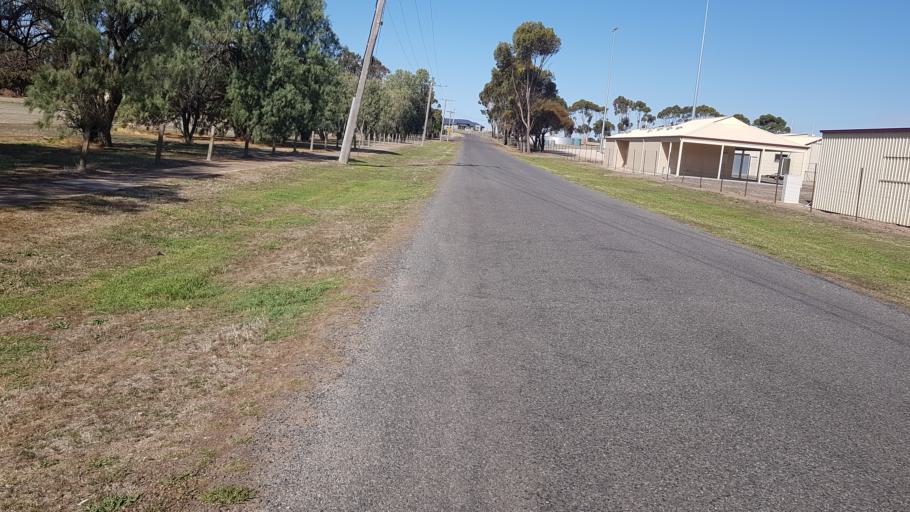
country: AU
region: Victoria
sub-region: Horsham
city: Horsham
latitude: -36.7419
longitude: 141.9477
